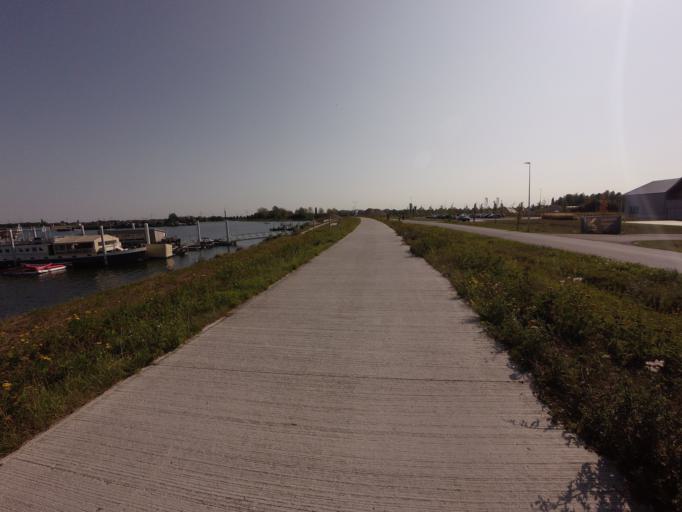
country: BE
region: Flanders
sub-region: Provincie Limburg
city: Maaseik
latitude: 51.1384
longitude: 5.8199
